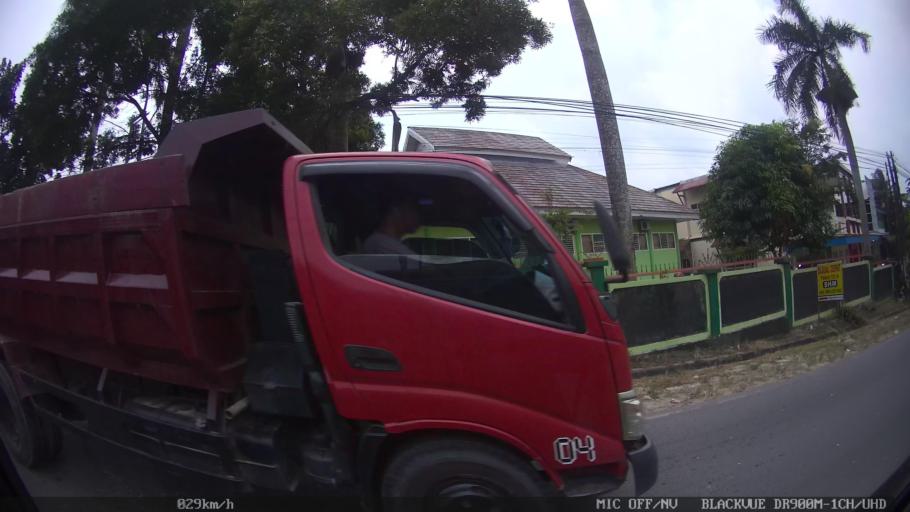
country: ID
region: Lampung
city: Kedaton
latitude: -5.3993
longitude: 105.3066
